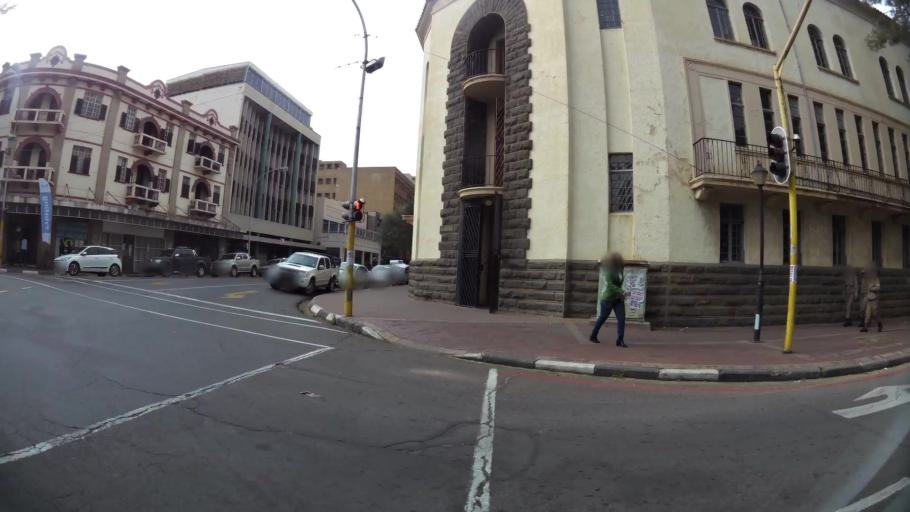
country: ZA
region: Orange Free State
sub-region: Mangaung Metropolitan Municipality
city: Bloemfontein
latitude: -29.1169
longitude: 26.2168
